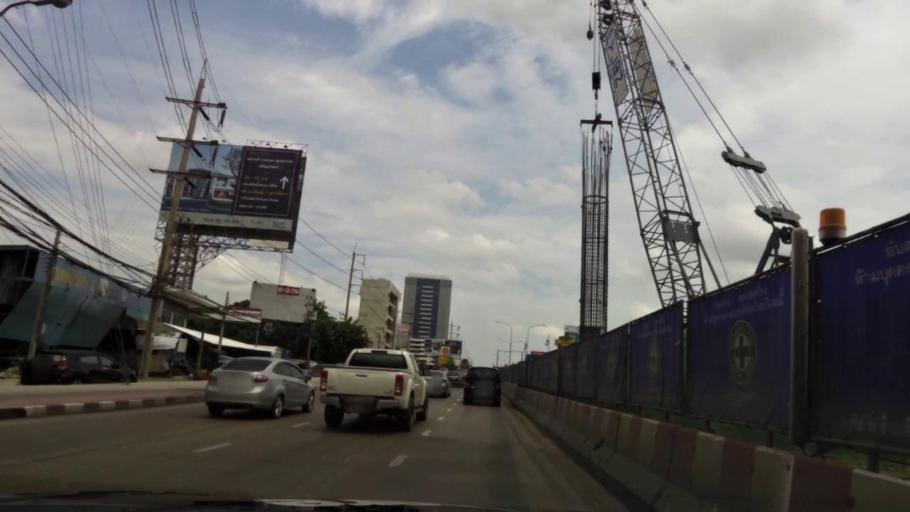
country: TH
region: Bangkok
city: Suan Luang
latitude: 13.7252
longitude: 100.6418
